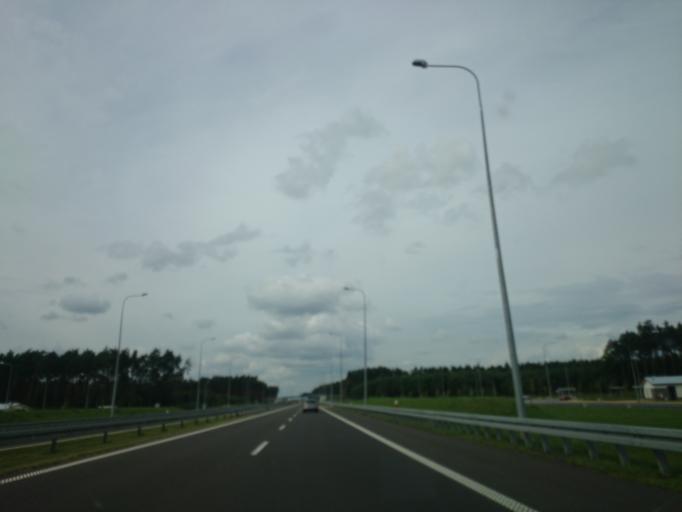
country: PL
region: West Pomeranian Voivodeship
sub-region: Powiat pyrzycki
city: Bielice
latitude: 53.1513
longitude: 14.7133
